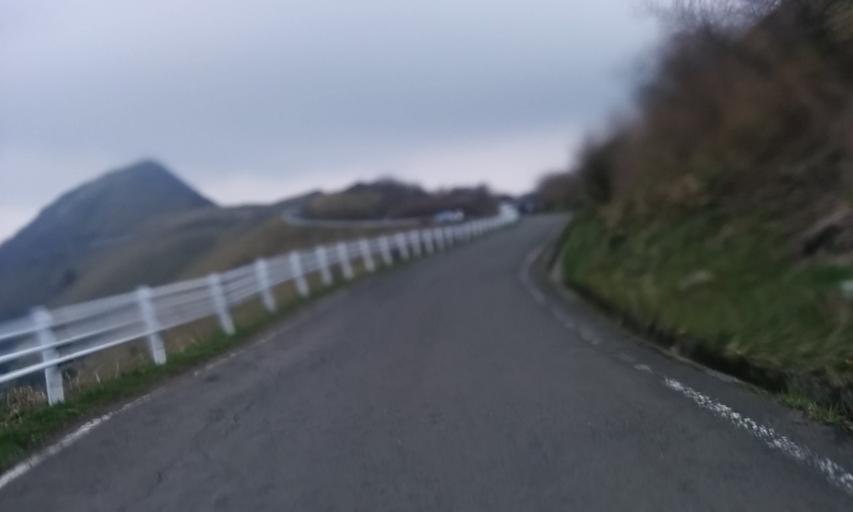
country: JP
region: Ehime
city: Saijo
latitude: 33.7837
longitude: 133.2313
